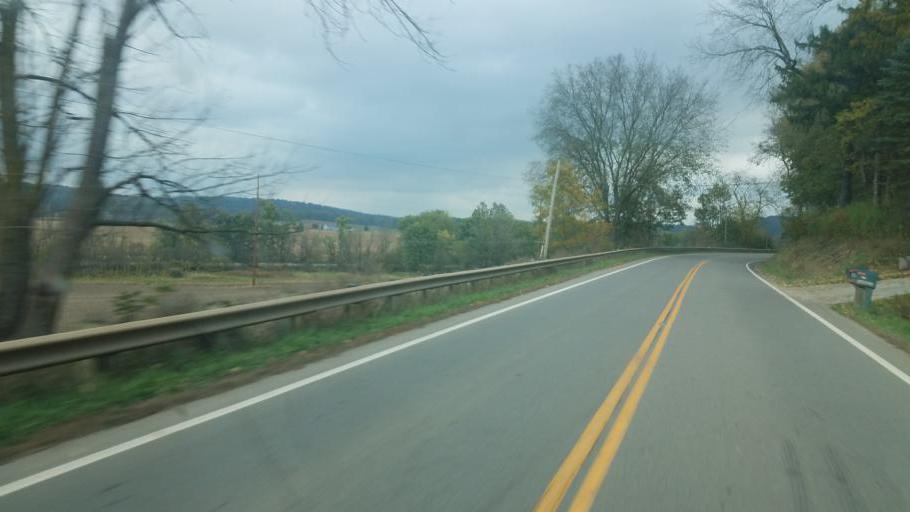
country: US
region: Ohio
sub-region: Ashland County
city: Loudonville
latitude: 40.6534
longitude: -82.2669
